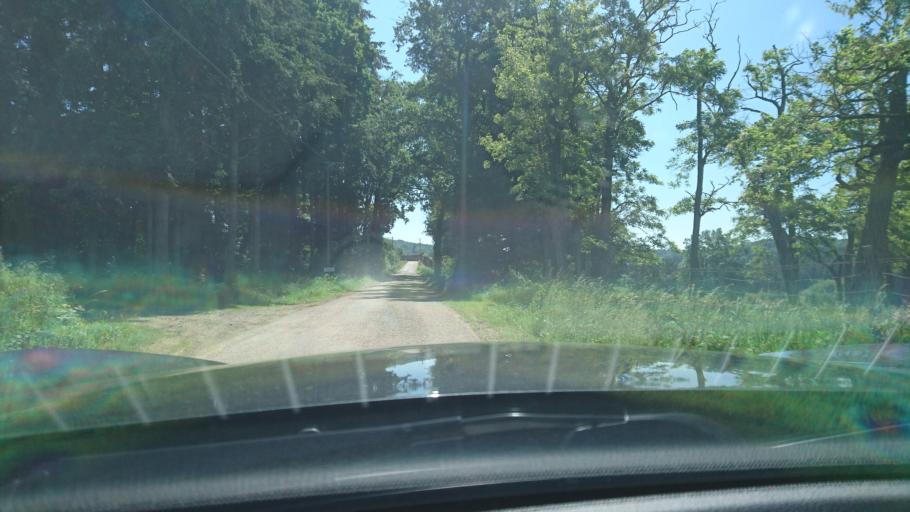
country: FR
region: Rhone-Alpes
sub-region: Departement de la Loire
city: Bussieres
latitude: 45.8573
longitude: 4.2444
